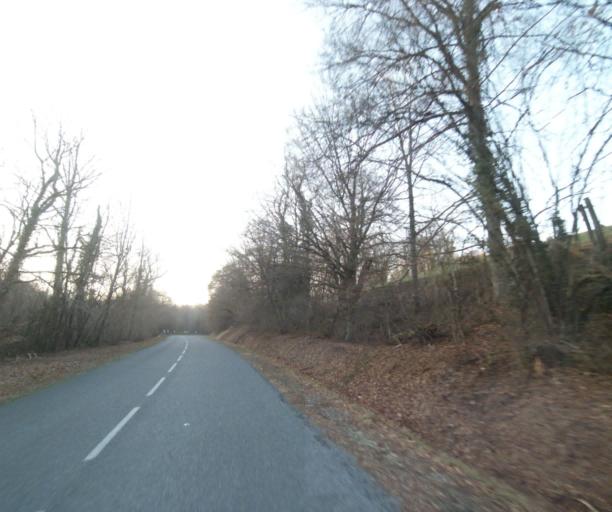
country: FR
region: Champagne-Ardenne
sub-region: Departement de la Haute-Marne
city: Bienville
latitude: 48.6115
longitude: 5.0642
